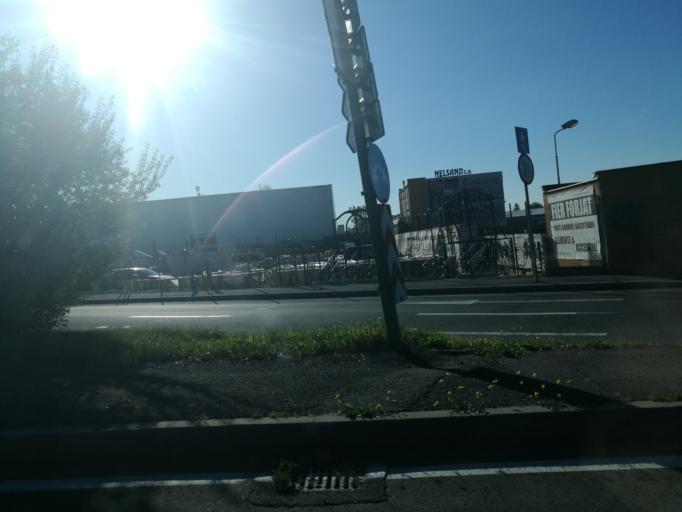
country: RO
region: Brasov
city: Brasov
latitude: 45.6701
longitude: 25.5907
